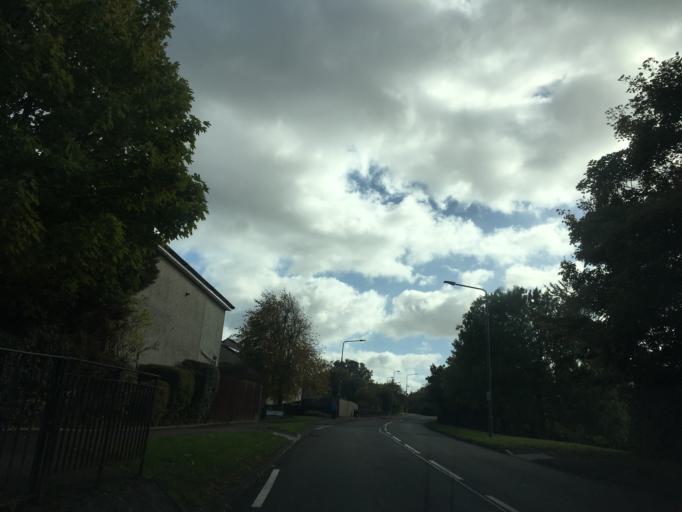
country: GB
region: Scotland
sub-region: Edinburgh
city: Currie
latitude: 55.9542
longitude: -3.3068
